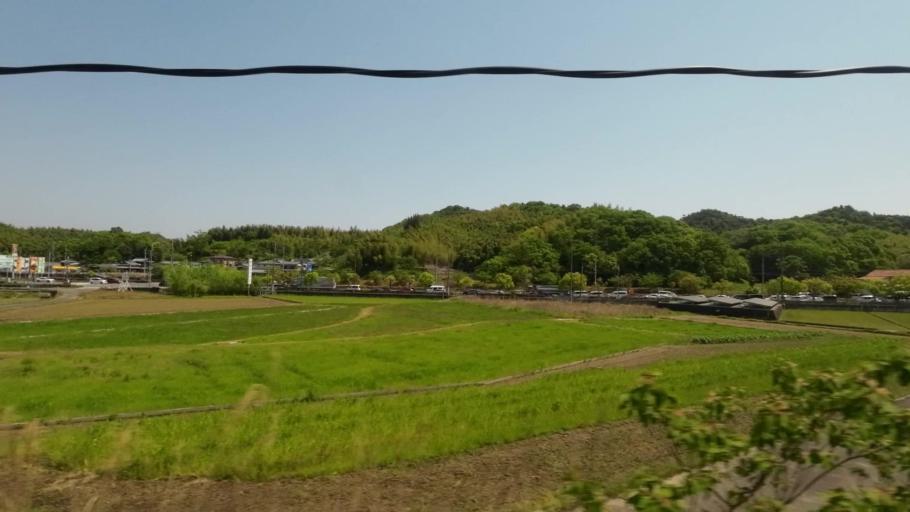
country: JP
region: Ehime
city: Saijo
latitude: 33.9992
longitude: 133.0397
